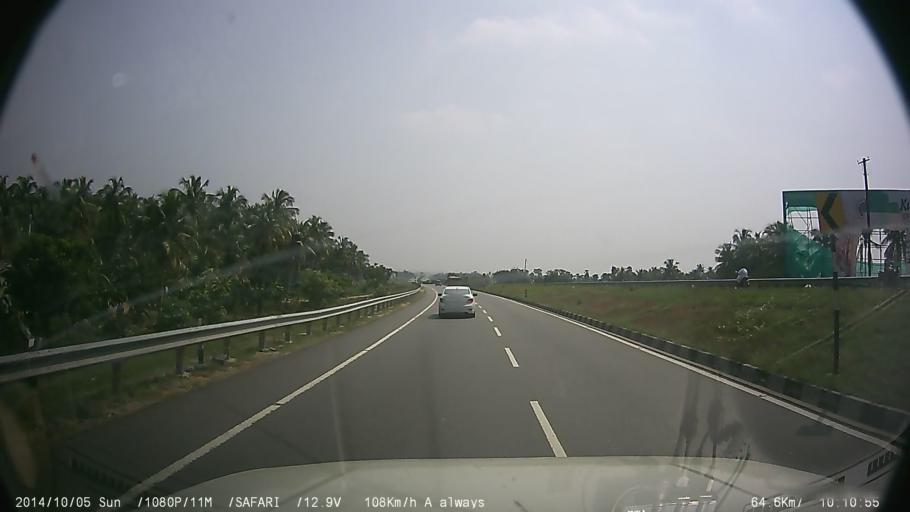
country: IN
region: Tamil Nadu
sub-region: Salem
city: Konganapuram
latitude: 11.5363
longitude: 77.9647
